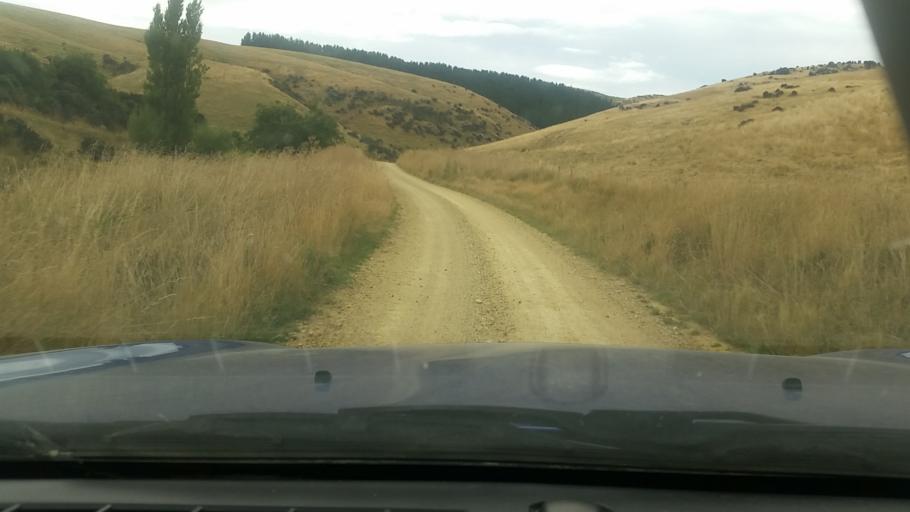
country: NZ
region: Southland
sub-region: Gore District
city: Gore
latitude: -45.5916
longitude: 169.3883
